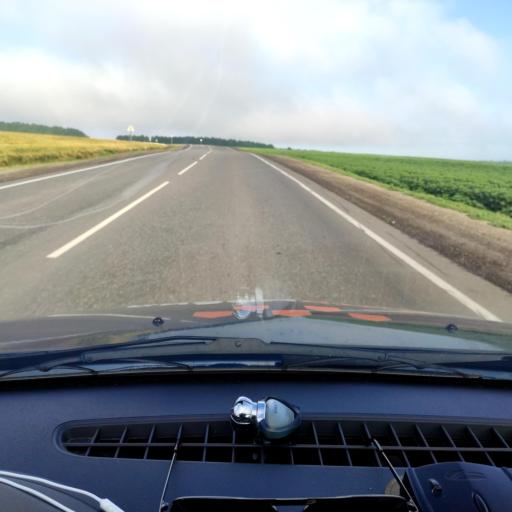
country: RU
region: Orjol
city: Livny
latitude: 52.4477
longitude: 37.4631
